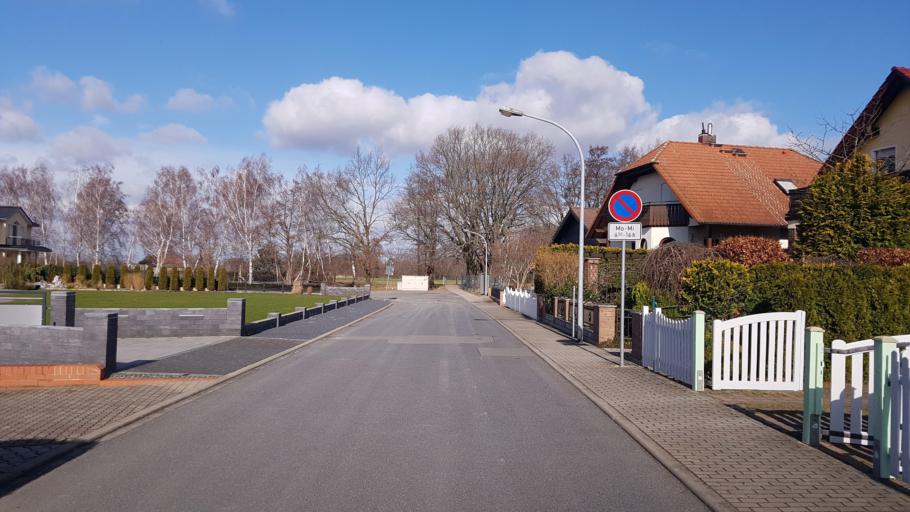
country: DE
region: Brandenburg
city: Herzberg
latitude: 51.7012
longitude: 13.2299
